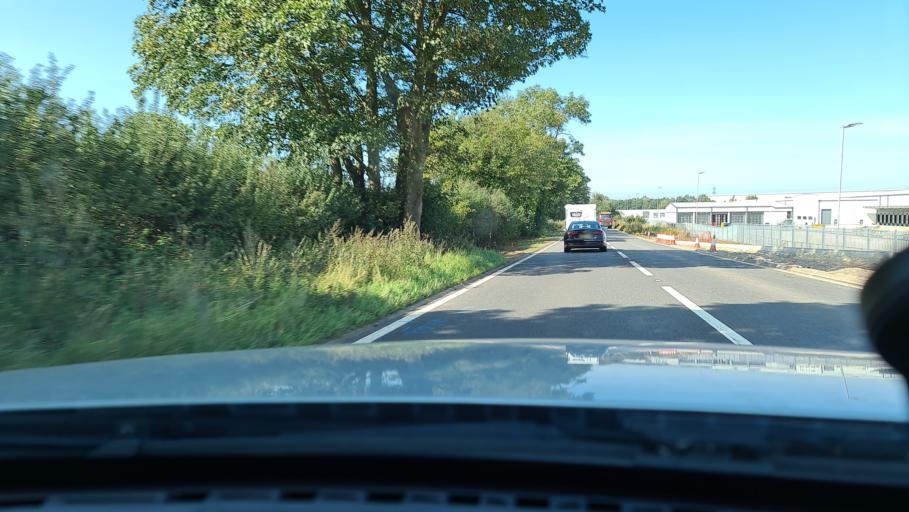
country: GB
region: England
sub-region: Leicestershire
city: Hinckley
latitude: 52.5083
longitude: -1.3424
